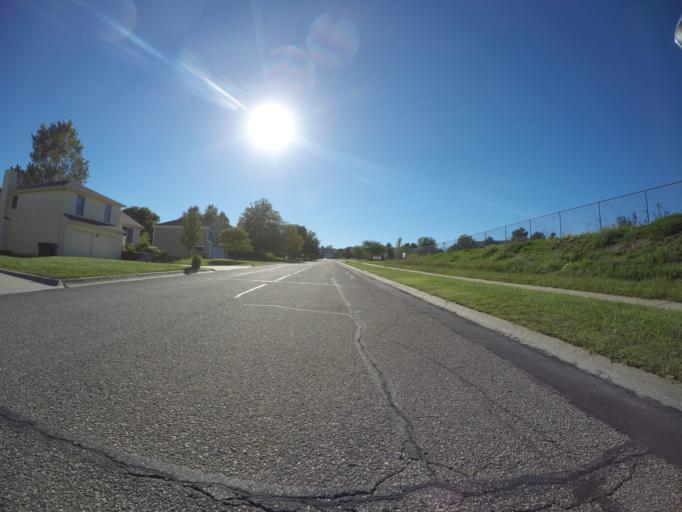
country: US
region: Kansas
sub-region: Riley County
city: Manhattan
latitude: 39.2117
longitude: -96.6229
